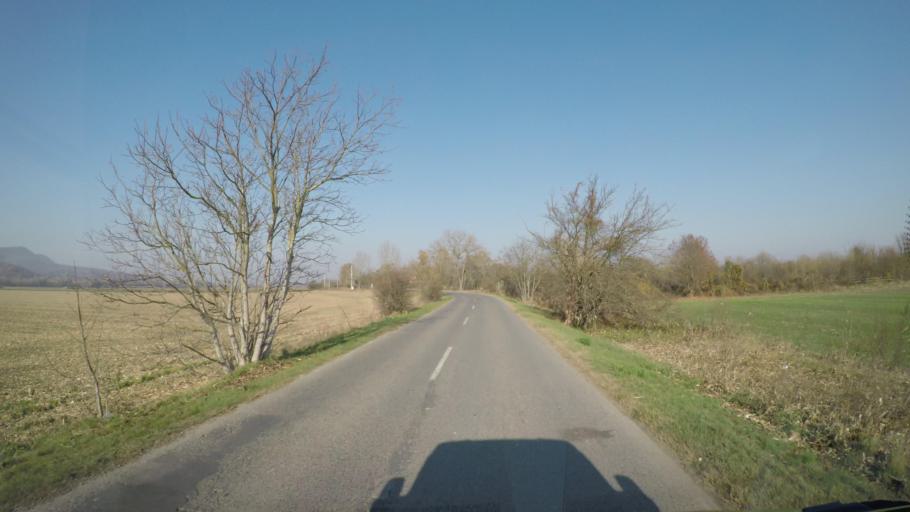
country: HU
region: Pest
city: Leanyfalu
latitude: 47.6938
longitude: 19.1037
